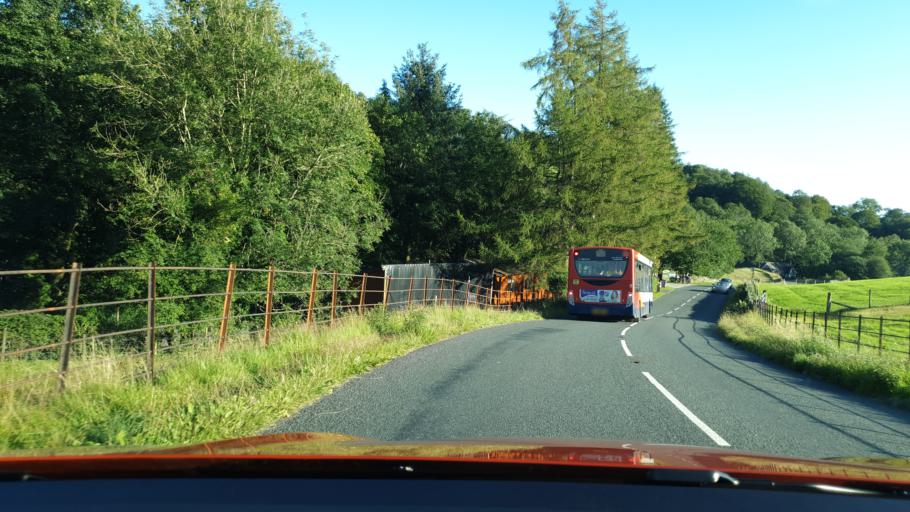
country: GB
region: England
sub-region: Cumbria
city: Windermere
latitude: 54.4199
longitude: -2.9043
